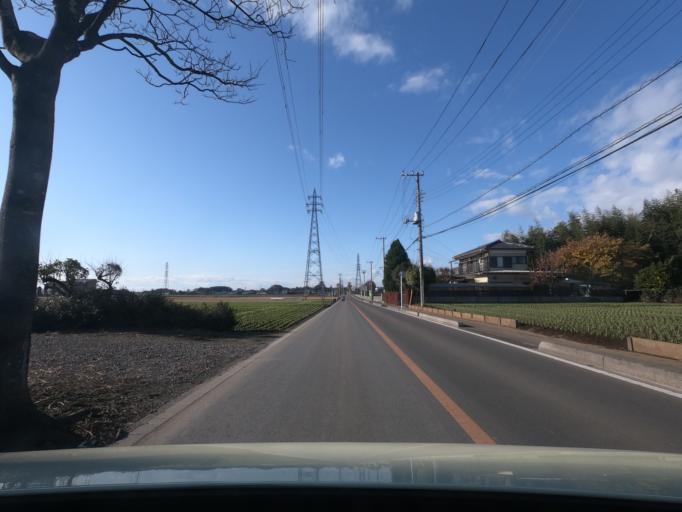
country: JP
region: Ibaraki
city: Koga
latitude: 36.2403
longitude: 139.7439
